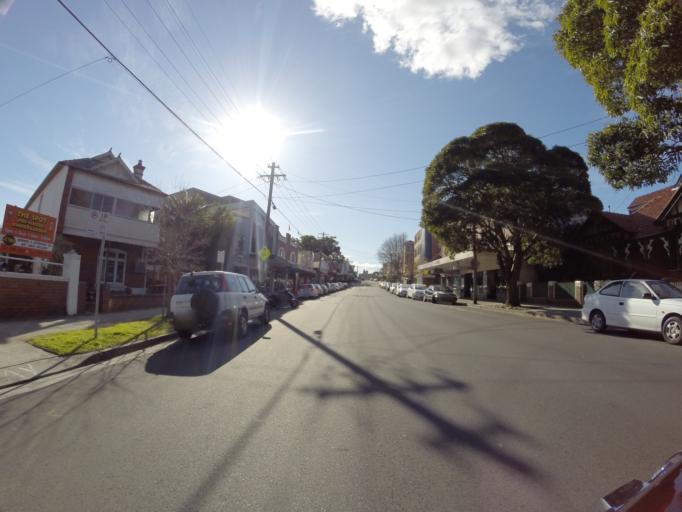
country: AU
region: New South Wales
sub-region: Randwick
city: Randwick
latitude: -33.9212
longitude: 151.2430
